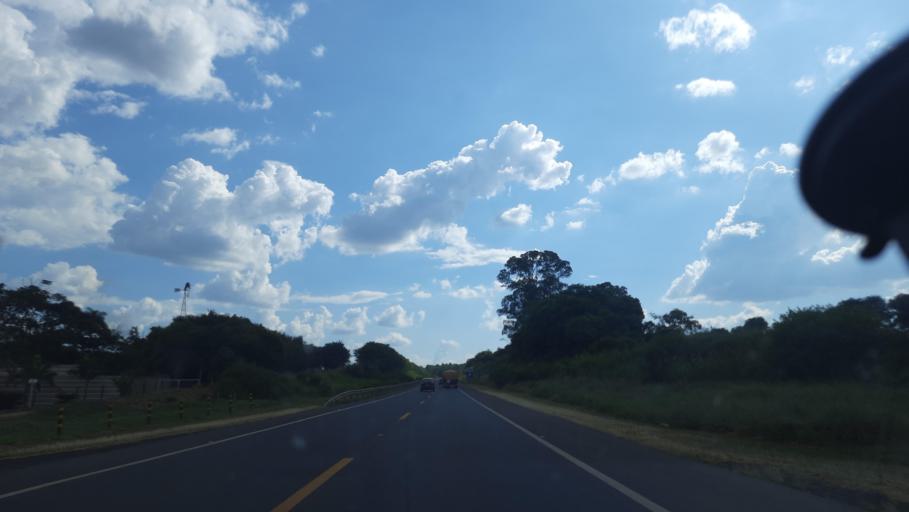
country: BR
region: Sao Paulo
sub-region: Casa Branca
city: Casa Branca
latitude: -21.7508
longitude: -46.9943
